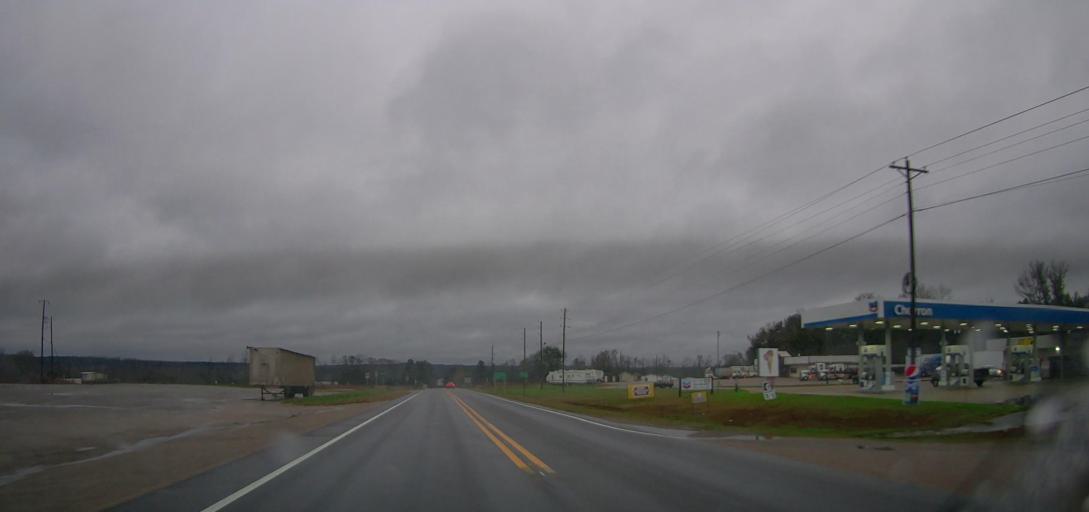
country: US
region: Alabama
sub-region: Chilton County
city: Thorsby
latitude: 32.7707
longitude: -86.8809
